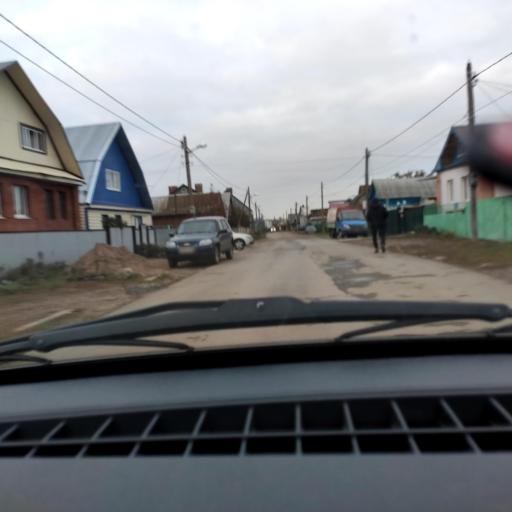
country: RU
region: Bashkortostan
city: Ufa
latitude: 54.7455
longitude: 55.9068
